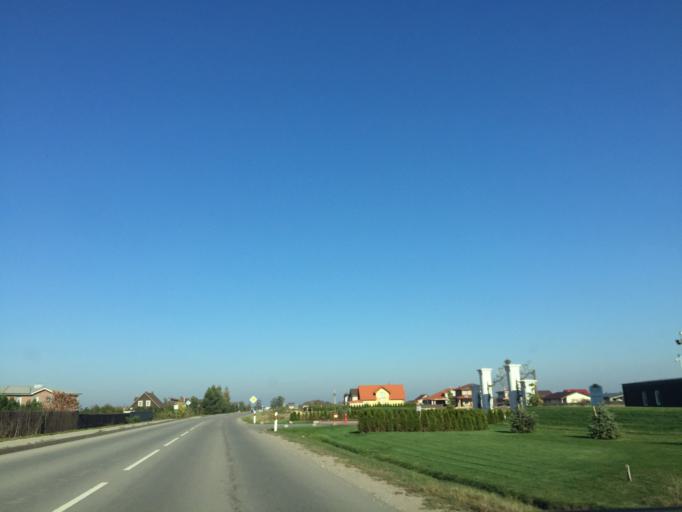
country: LT
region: Klaipedos apskritis
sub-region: Klaipeda
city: Klaipeda
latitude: 55.7433
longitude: 21.1923
